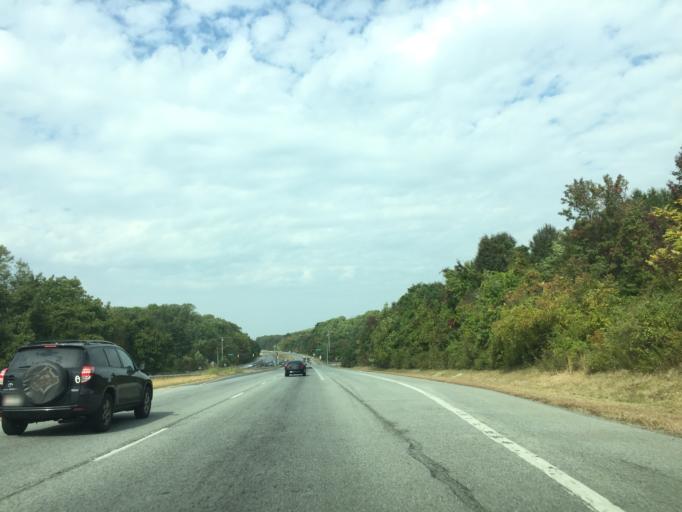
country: US
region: Maryland
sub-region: Harford County
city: Bel Air South
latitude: 39.4764
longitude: -76.3181
